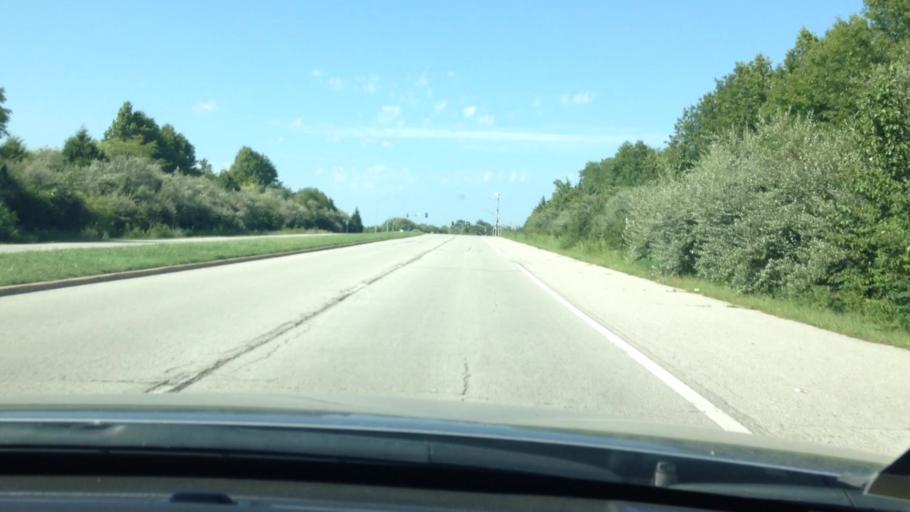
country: US
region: Missouri
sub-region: Jackson County
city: Grandview
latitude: 38.9132
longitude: -94.4819
